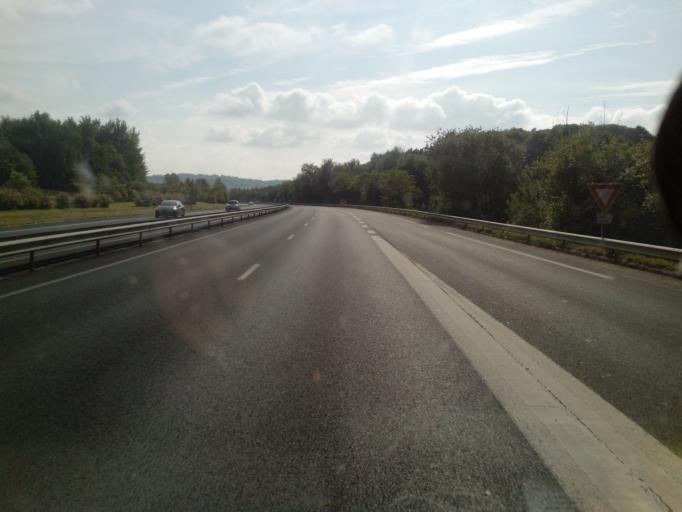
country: FR
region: Haute-Normandie
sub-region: Departement de la Seine-Maritime
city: Neufchatel-en-Bray
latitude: 49.7197
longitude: 1.4235
